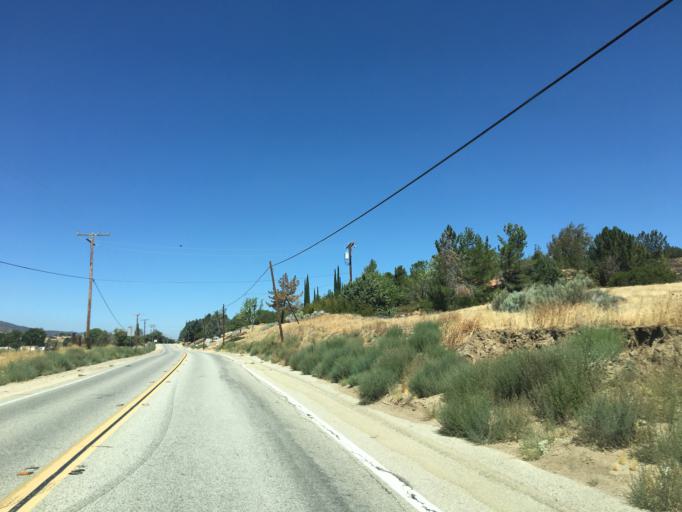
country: US
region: California
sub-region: Los Angeles County
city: Leona Valley
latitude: 34.6136
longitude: -118.2758
